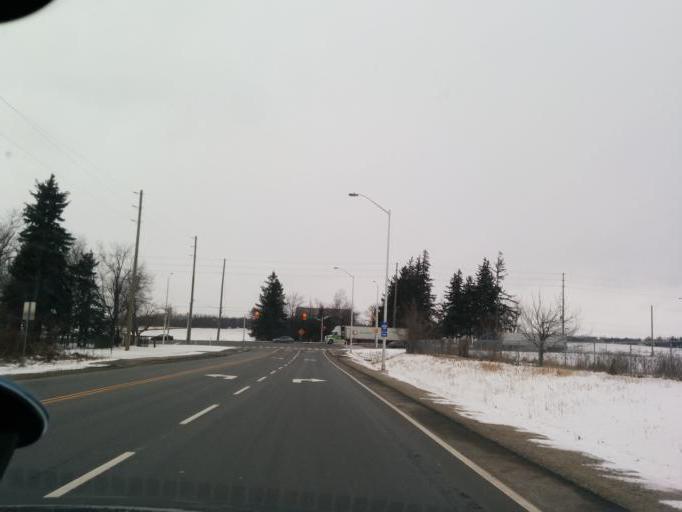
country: CA
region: Ontario
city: Brampton
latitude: 43.5930
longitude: -79.8120
